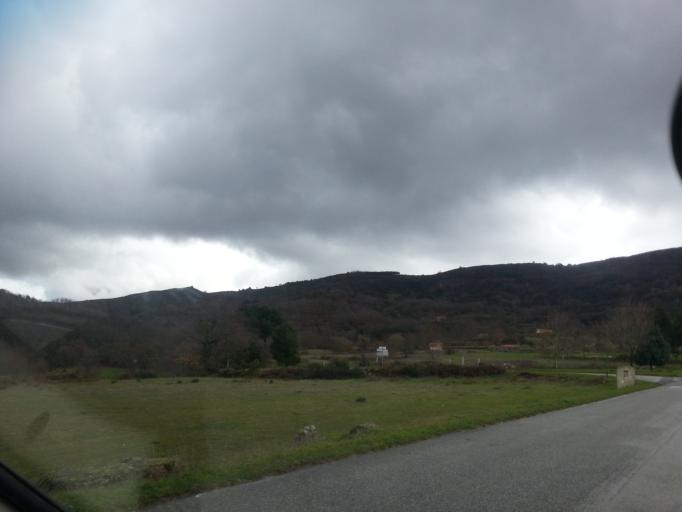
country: PT
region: Guarda
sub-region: Celorico da Beira
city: Celorico da Beira
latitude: 40.5495
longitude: -7.4564
